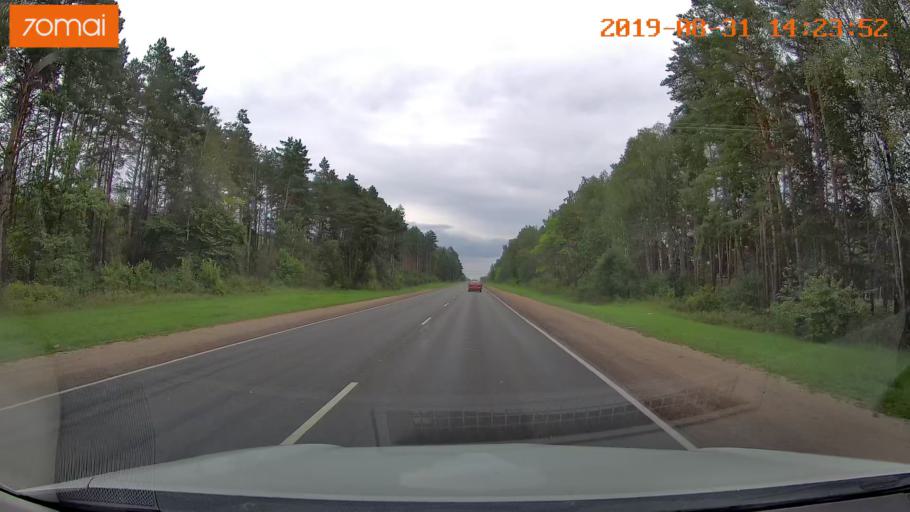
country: RU
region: Smolensk
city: Yekimovichi
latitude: 54.0993
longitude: 33.2433
